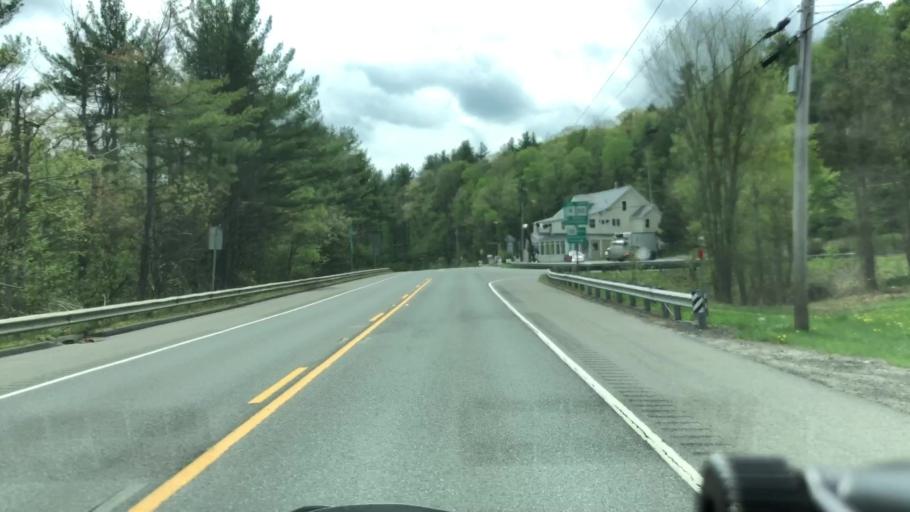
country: US
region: Massachusetts
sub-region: Hampshire County
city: Chesterfield
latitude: 42.4651
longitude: -72.9055
